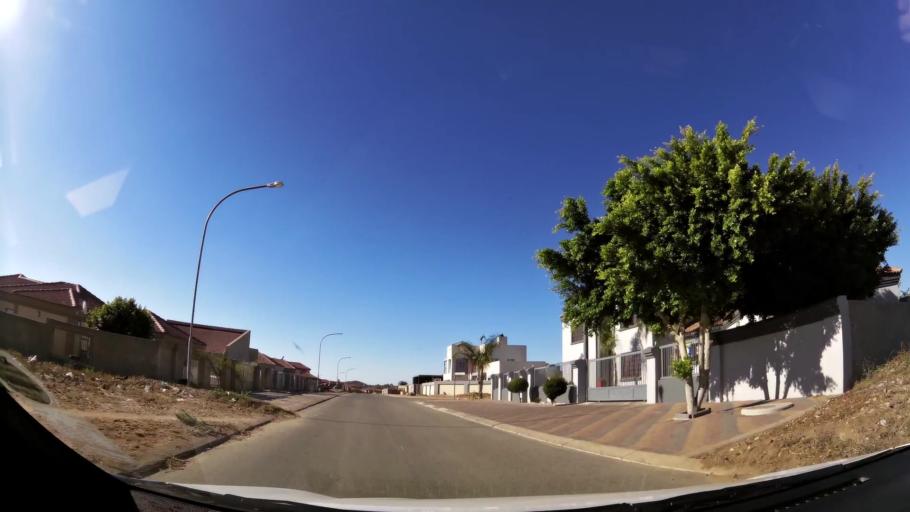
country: ZA
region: Limpopo
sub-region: Capricorn District Municipality
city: Polokwane
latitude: -23.9120
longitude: 29.5072
